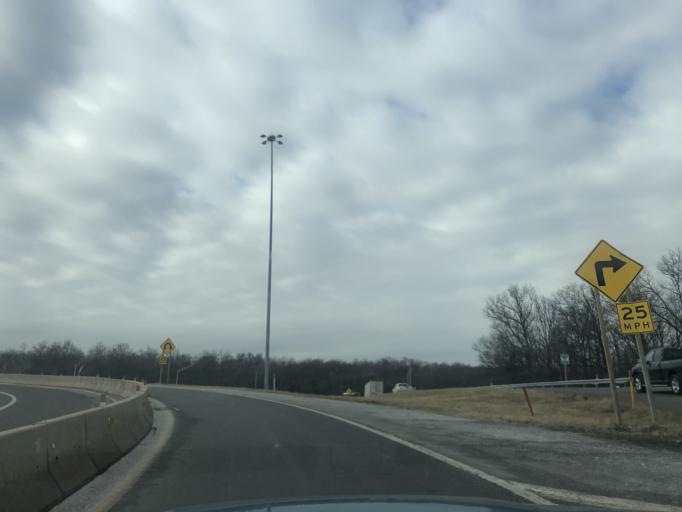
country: US
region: Pennsylvania
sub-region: Bucks County
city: Spinnerstown
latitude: 40.4382
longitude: -75.4248
